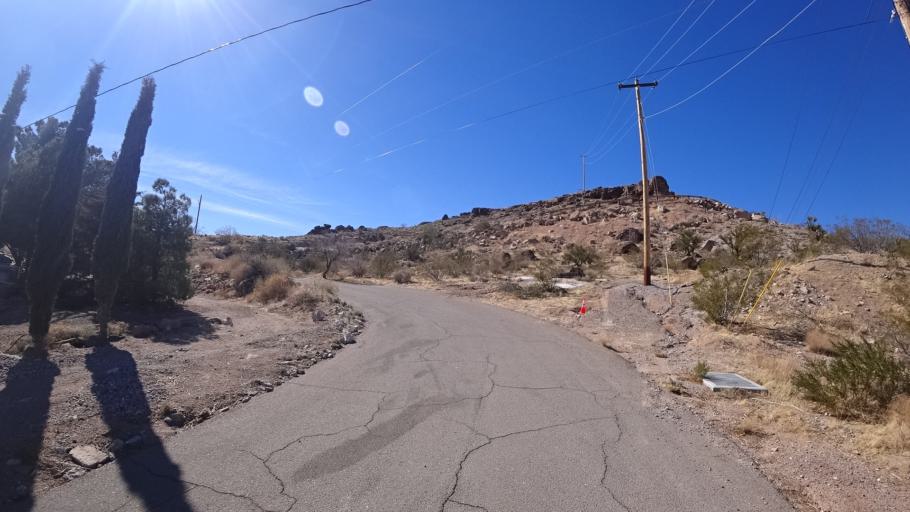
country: US
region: Arizona
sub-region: Mohave County
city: Kingman
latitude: 35.1965
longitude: -114.0382
